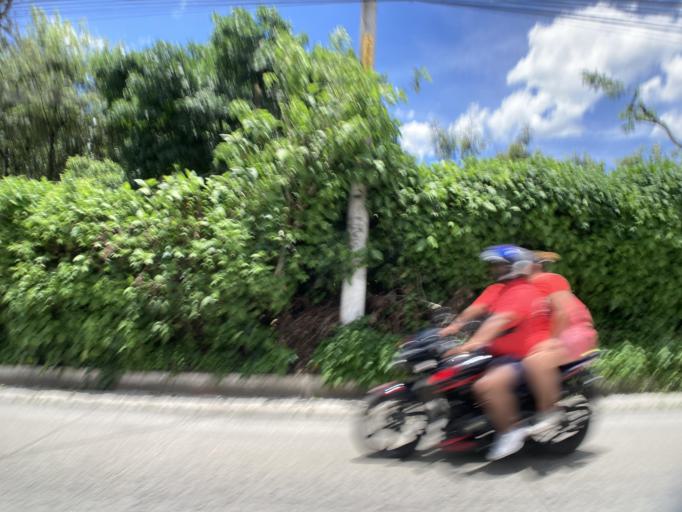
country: GT
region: Sacatepequez
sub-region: Municipio de Santa Maria de Jesus
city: Santa Maria de Jesus
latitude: 14.5374
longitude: -90.7296
